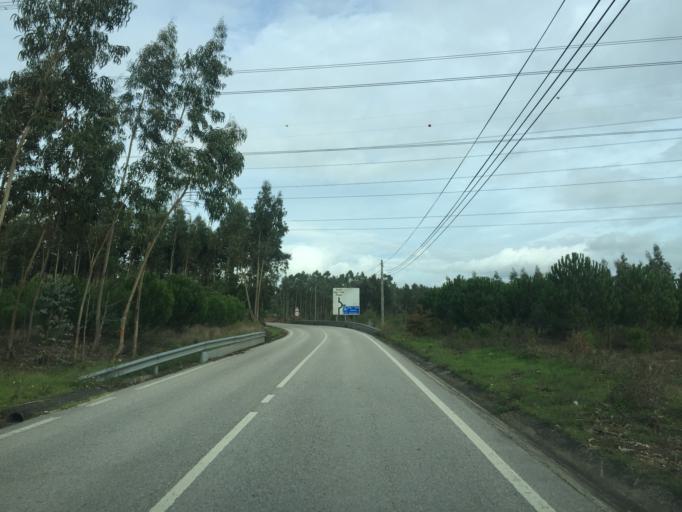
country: PT
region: Coimbra
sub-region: Figueira da Foz
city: Lavos
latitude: 40.0467
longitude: -8.8168
